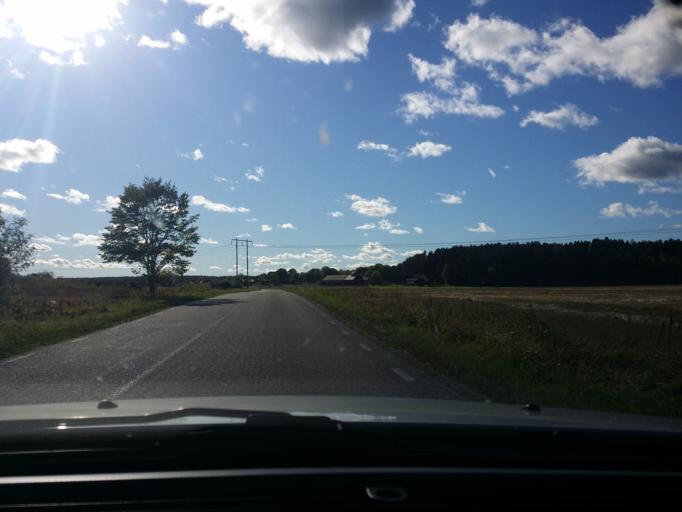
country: SE
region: Vaestmanland
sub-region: Vasteras
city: Vasteras
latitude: 59.5493
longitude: 16.4554
